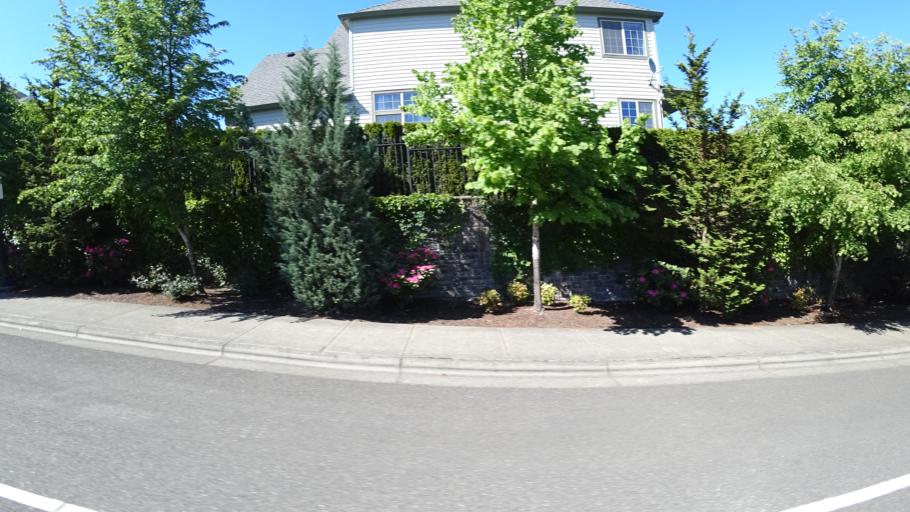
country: US
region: Oregon
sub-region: Washington County
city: Oak Hills
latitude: 45.5559
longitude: -122.8151
